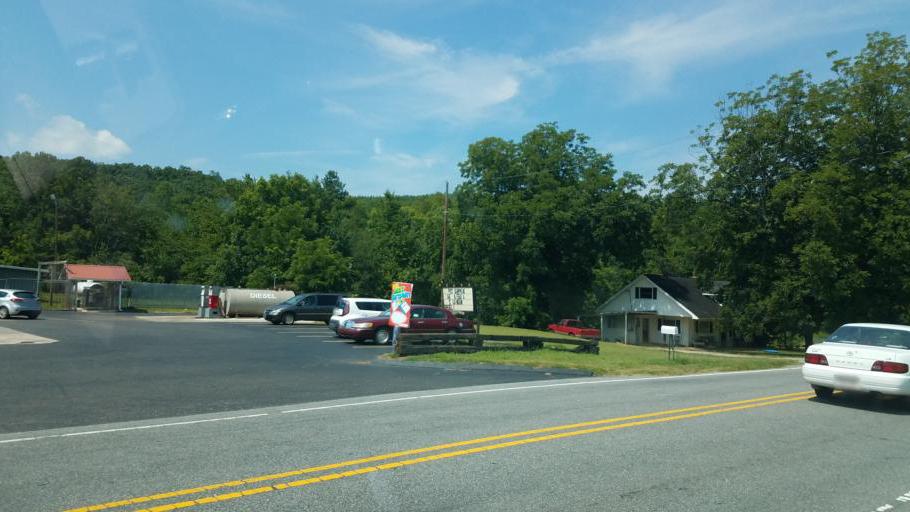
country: US
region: North Carolina
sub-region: Burke County
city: Icard
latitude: 35.5559
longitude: -81.5058
